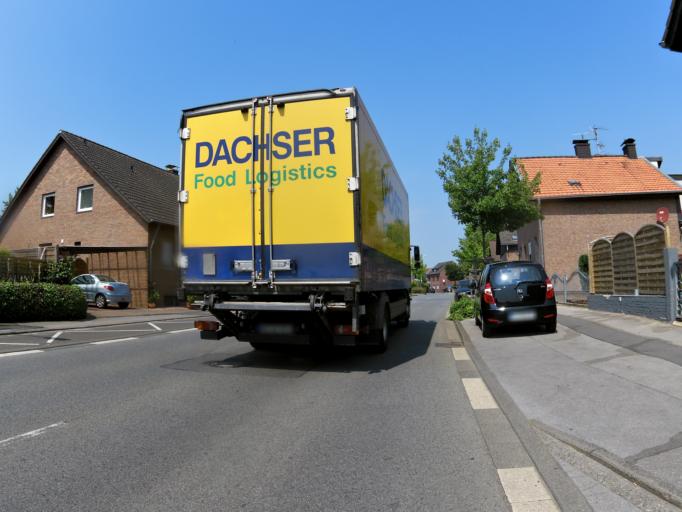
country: DE
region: North Rhine-Westphalia
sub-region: Regierungsbezirk Koln
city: Wurselen
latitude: 50.8262
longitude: 6.0981
